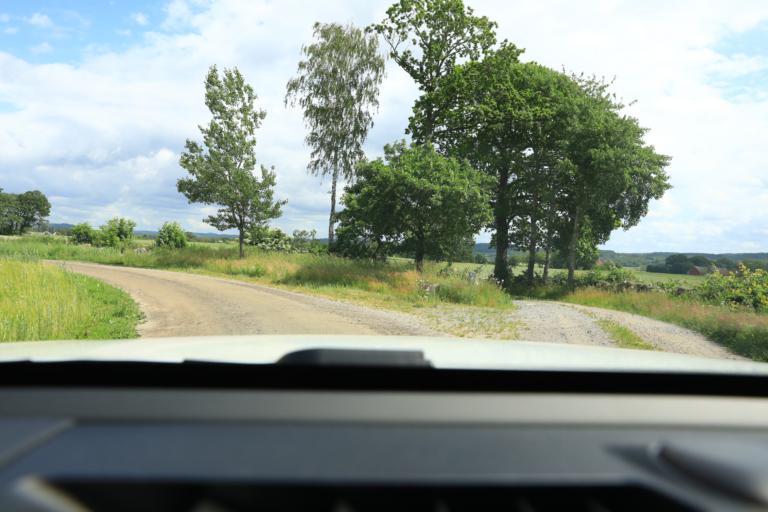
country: SE
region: Halland
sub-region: Varbergs Kommun
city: Tvaaker
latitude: 57.0999
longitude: 12.4011
